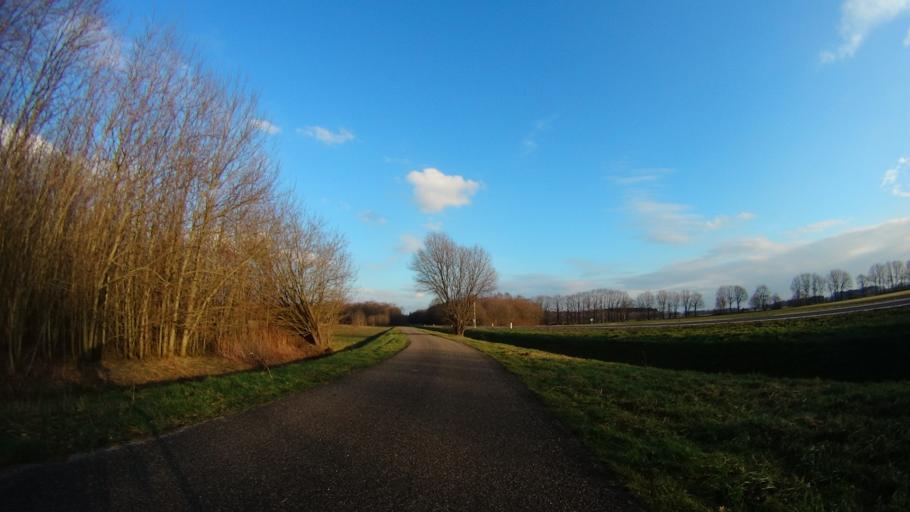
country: NL
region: Drenthe
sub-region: Gemeente Coevorden
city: Sleen
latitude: 52.8014
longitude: 6.7515
